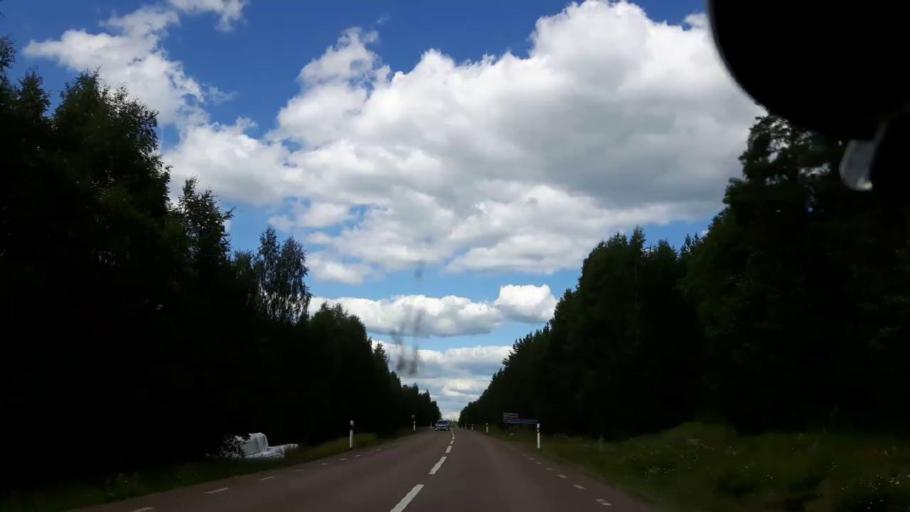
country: SE
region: Jaemtland
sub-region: Ragunda Kommun
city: Hammarstrand
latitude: 62.9231
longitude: 16.7026
